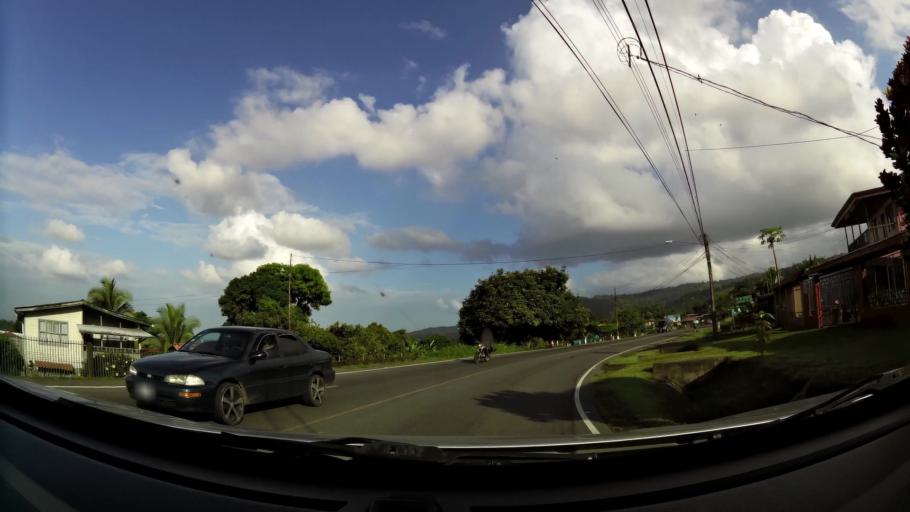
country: CR
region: Limon
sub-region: Canton de Siquirres
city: Siquirres
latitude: 10.0963
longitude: -83.5108
